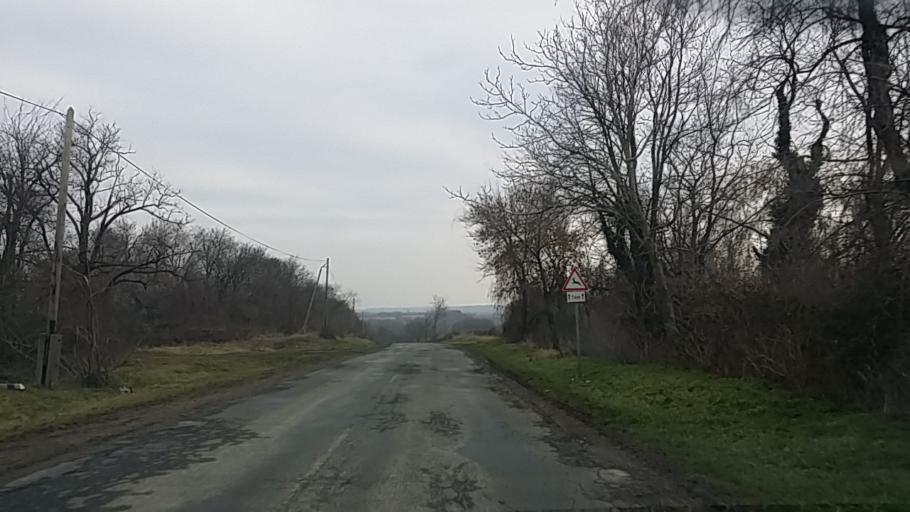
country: HU
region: Baranya
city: Pecsvarad
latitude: 46.1058
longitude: 18.5373
